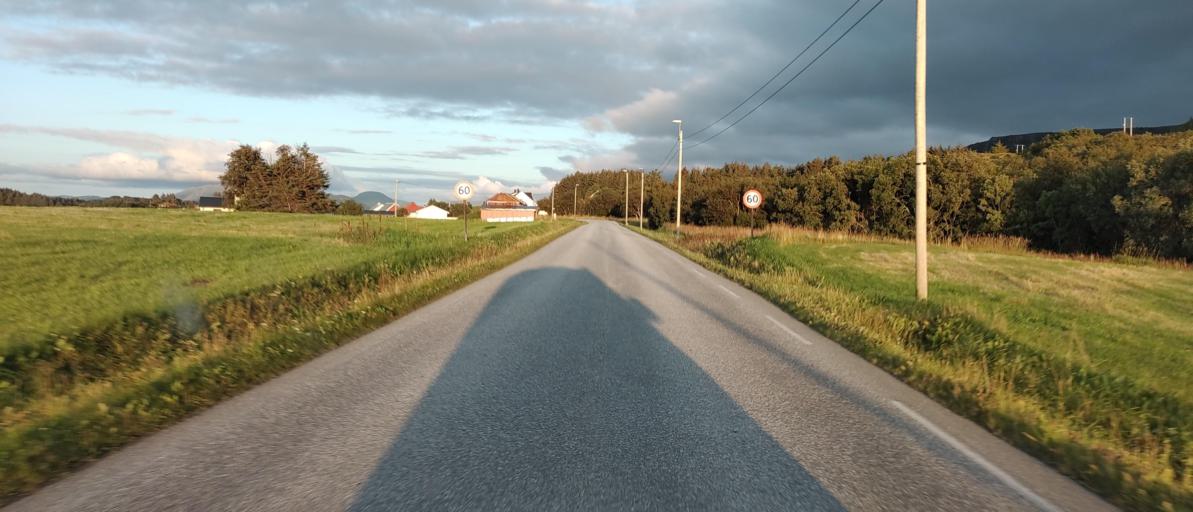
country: NO
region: More og Romsdal
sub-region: Fraena
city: Elnesvagen
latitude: 62.9895
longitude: 7.2023
